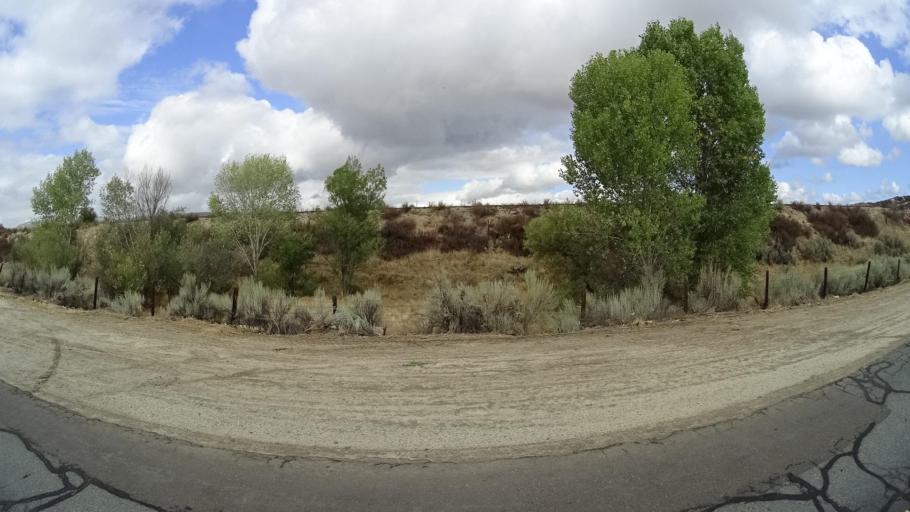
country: US
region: California
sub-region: San Diego County
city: Campo
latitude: 32.6273
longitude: -116.4621
